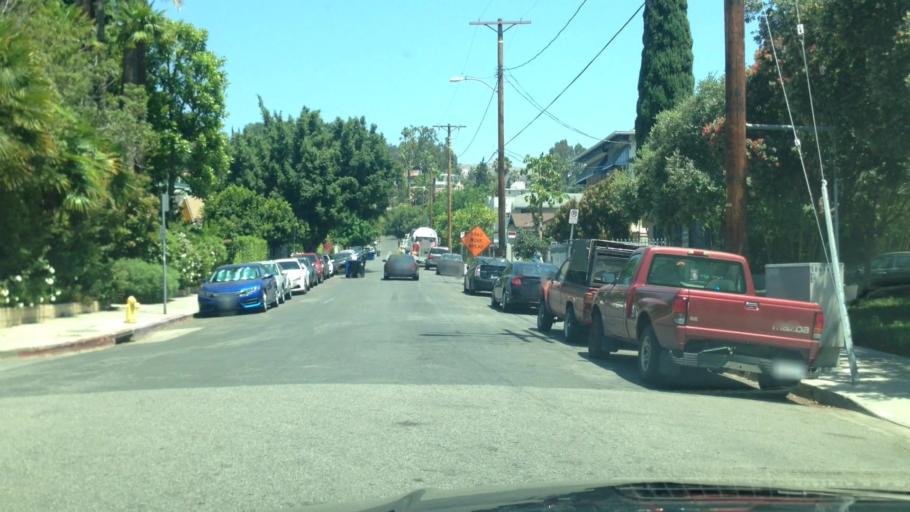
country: US
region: California
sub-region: Los Angeles County
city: Hollywood
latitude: 34.1056
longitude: -118.3240
